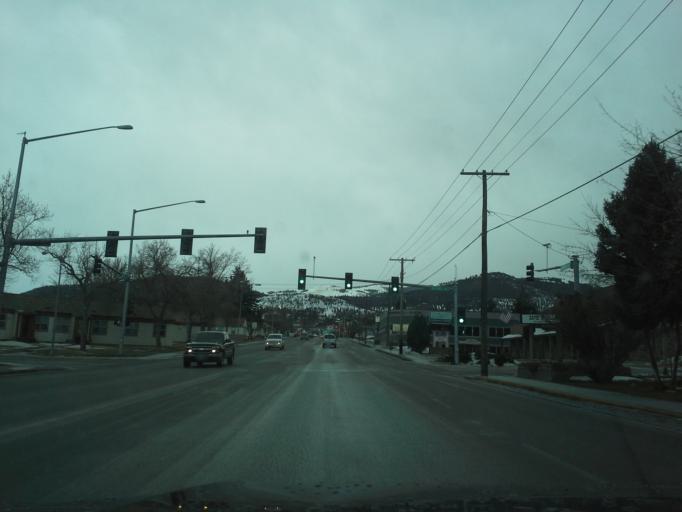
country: US
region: Montana
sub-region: Lewis and Clark County
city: Helena
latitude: 46.5946
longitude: -112.0205
